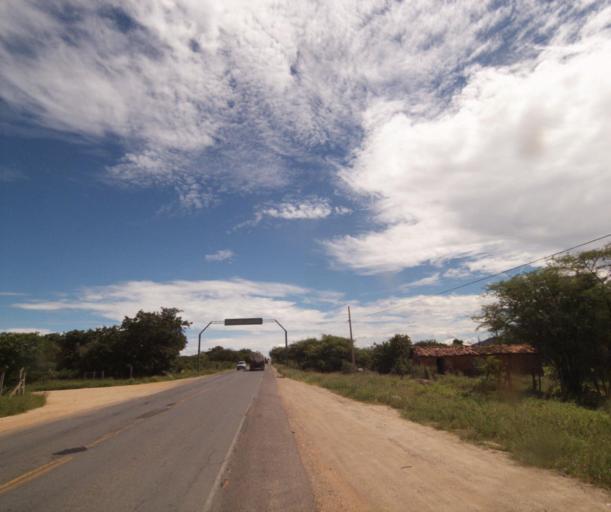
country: BR
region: Bahia
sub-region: Guanambi
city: Guanambi
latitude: -14.2496
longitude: -42.7818
